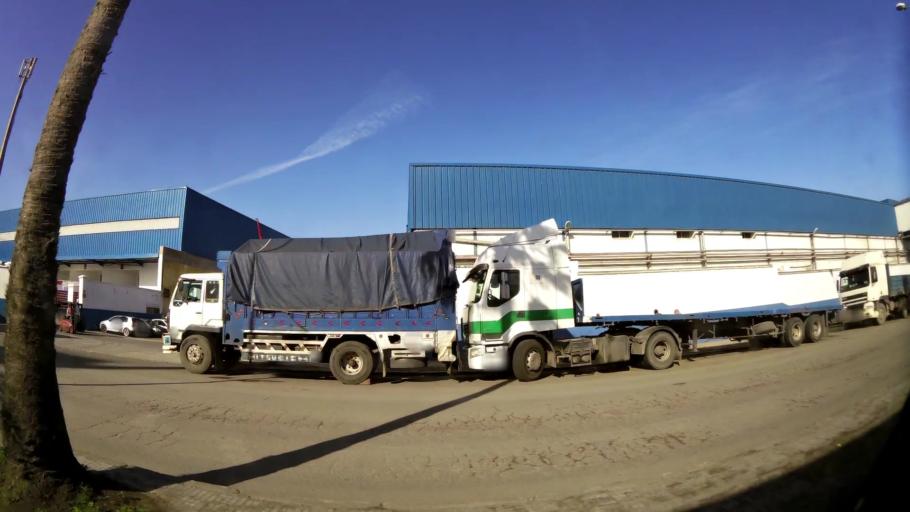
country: MA
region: Grand Casablanca
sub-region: Casablanca
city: Casablanca
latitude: 33.6023
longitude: -7.5737
